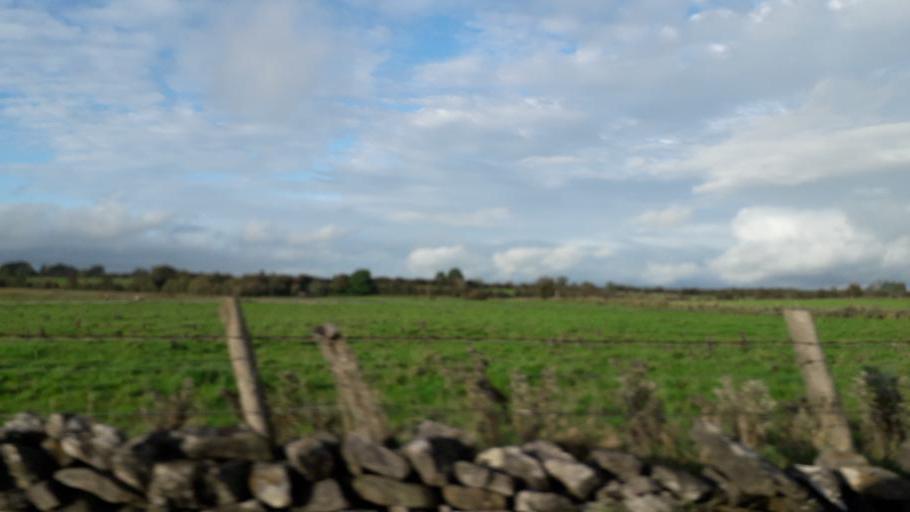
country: IE
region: Connaught
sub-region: Roscommon
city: Roscommon
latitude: 53.7680
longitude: -8.2106
